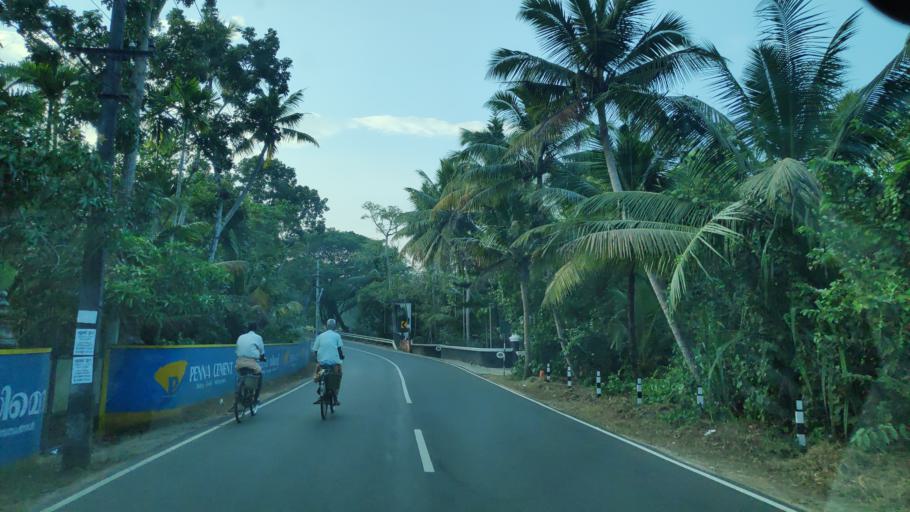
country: IN
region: Kerala
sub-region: Alappuzha
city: Shertallai
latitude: 9.6771
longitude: 76.3793
